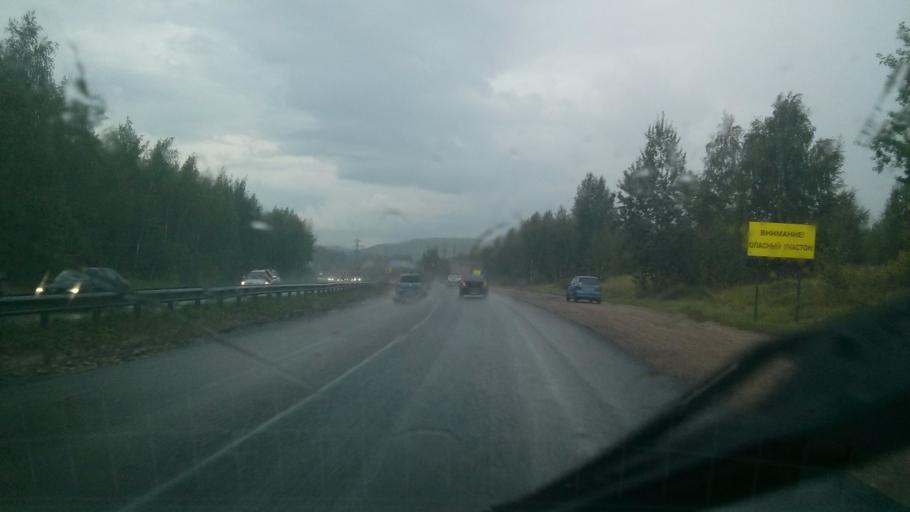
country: RU
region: Nizjnij Novgorod
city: Afonino
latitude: 56.2314
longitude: 44.0690
